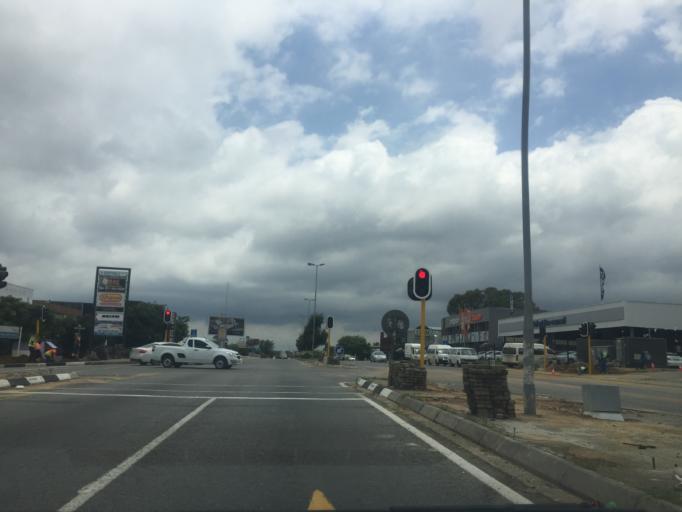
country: ZA
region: Gauteng
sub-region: City of Johannesburg Metropolitan Municipality
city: Modderfontein
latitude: -26.0903
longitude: 28.0794
